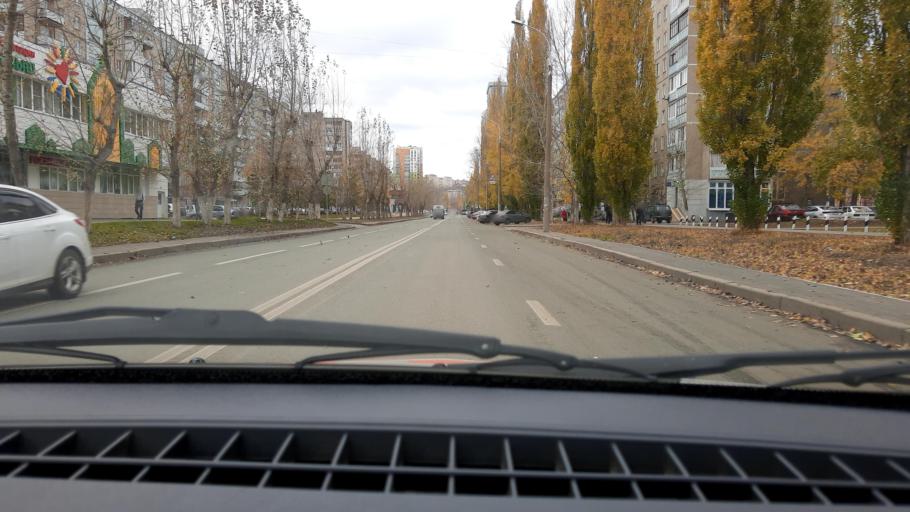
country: RU
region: Bashkortostan
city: Ufa
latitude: 54.7653
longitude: 56.0640
